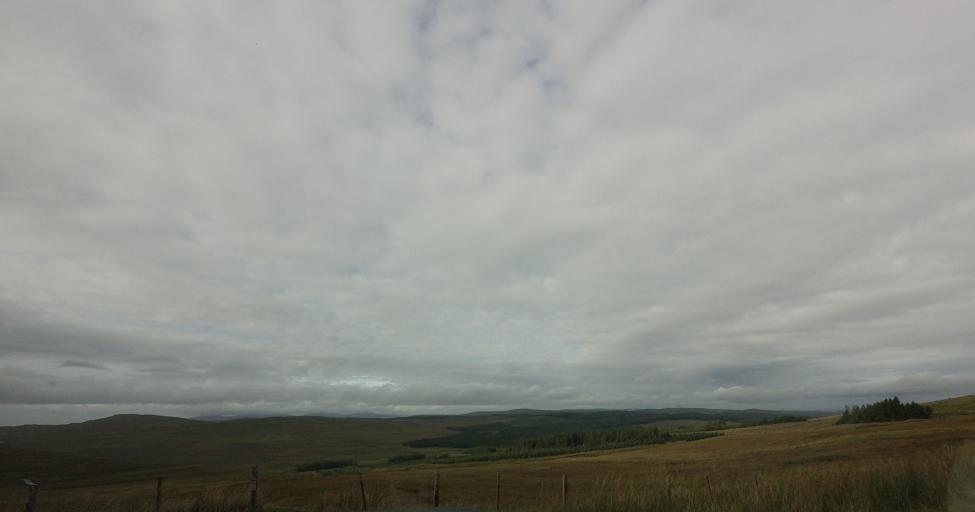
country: GB
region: Scotland
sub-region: Highland
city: Isle of Skye
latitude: 57.3964
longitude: -6.2711
